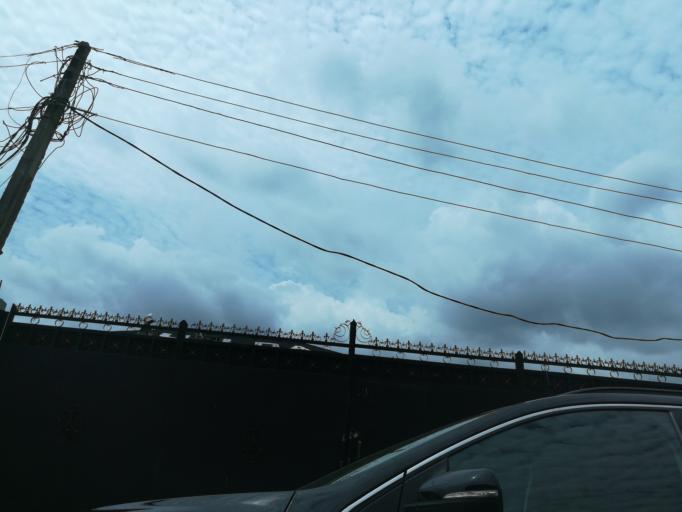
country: NG
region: Lagos
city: Oshodi
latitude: 6.5599
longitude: 3.3262
